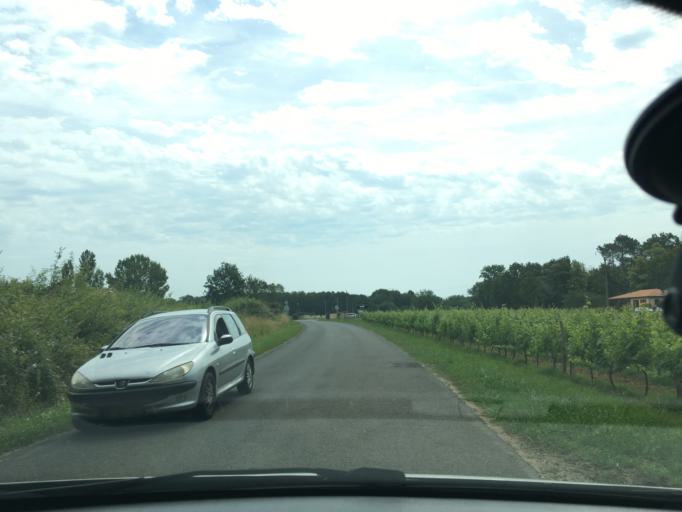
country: FR
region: Aquitaine
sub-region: Departement de la Gironde
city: Gaillan-en-Medoc
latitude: 45.3362
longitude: -0.9868
